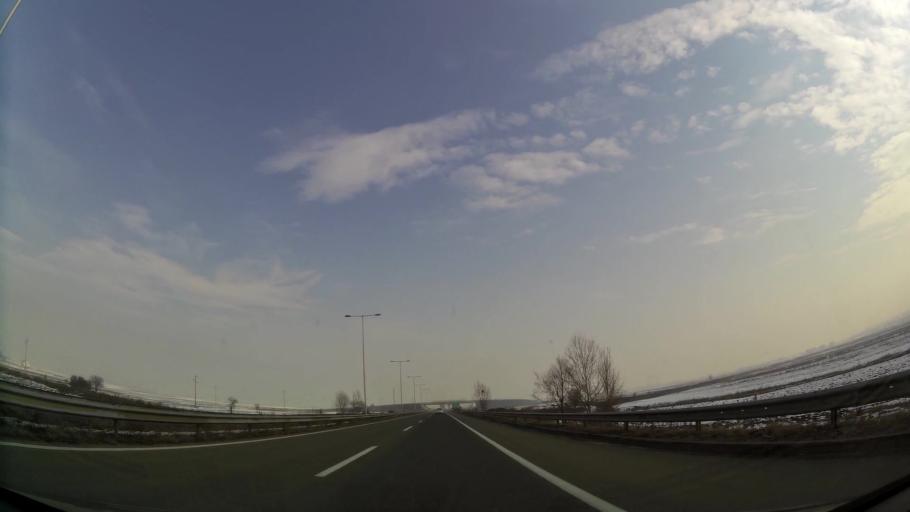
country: MK
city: Creshevo
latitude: 42.0324
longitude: 21.4939
